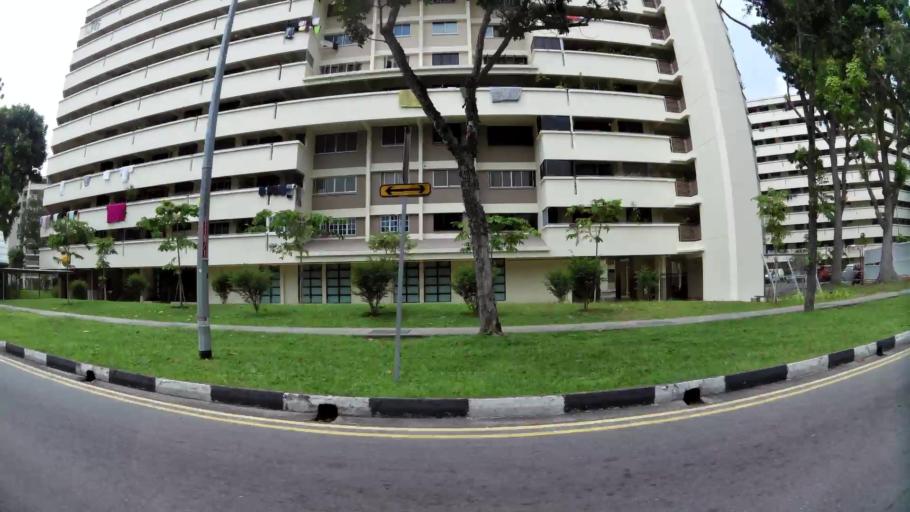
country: SG
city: Singapore
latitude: 1.3338
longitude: 103.9138
